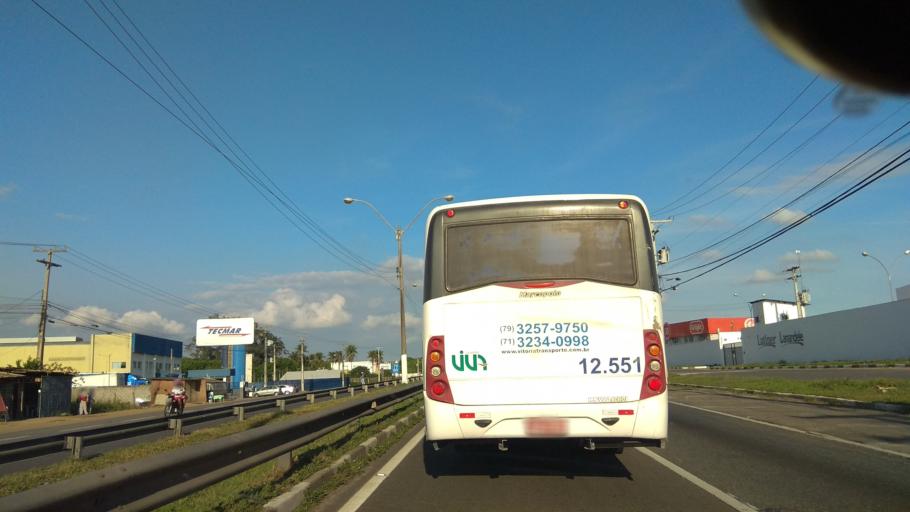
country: BR
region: Bahia
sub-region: Feira De Santana
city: Feira de Santana
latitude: -12.2929
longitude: -38.9083
